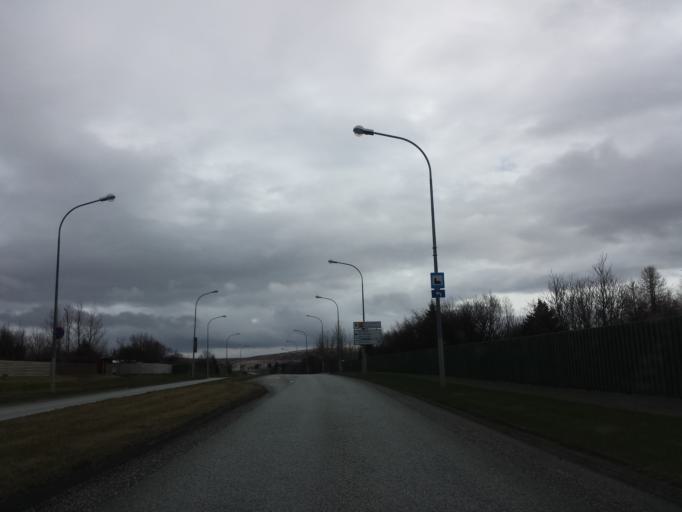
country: IS
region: Capital Region
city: Gardabaer
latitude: 64.0854
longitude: -21.9118
